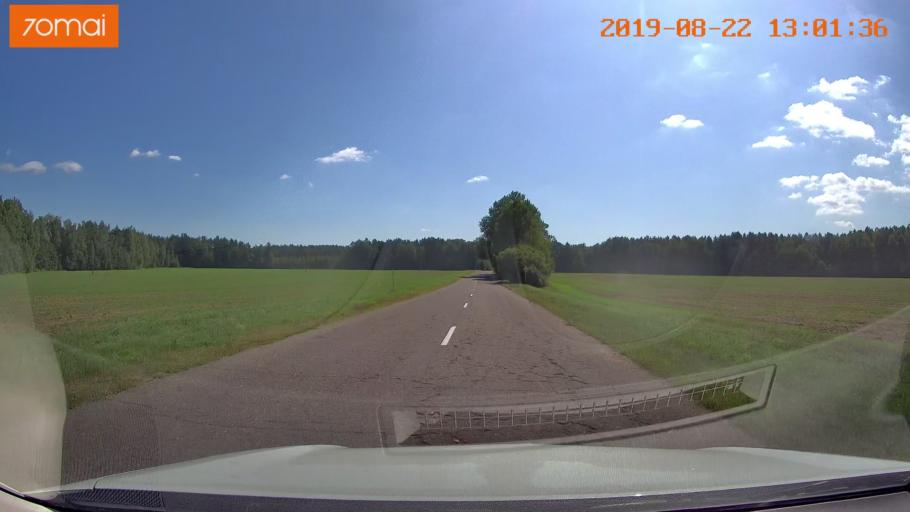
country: BY
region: Minsk
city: Prawdzinski
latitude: 53.3999
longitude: 27.8193
